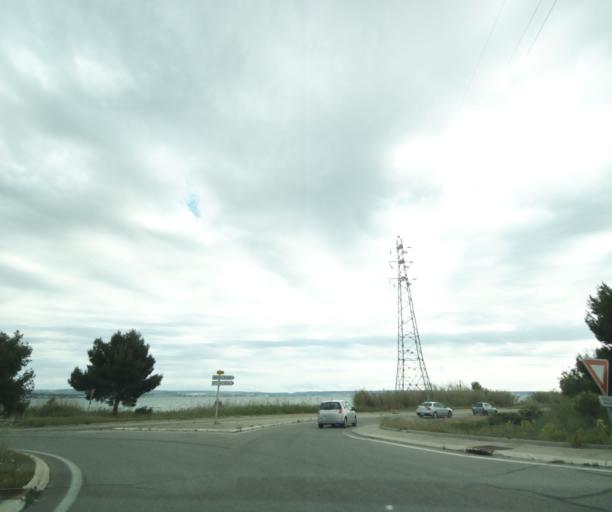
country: FR
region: Provence-Alpes-Cote d'Azur
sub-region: Departement des Bouches-du-Rhone
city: Rognac
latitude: 43.4924
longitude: 5.2045
